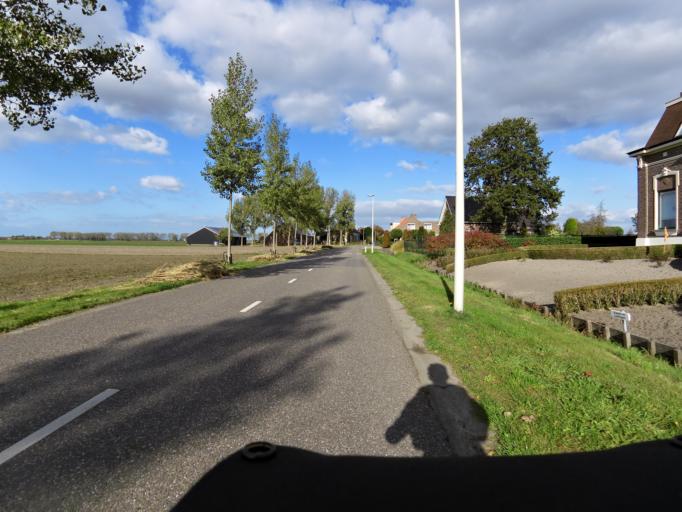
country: NL
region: North Brabant
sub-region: Gemeente Bergen op Zoom
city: Lepelstraat
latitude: 51.5603
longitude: 4.2643
